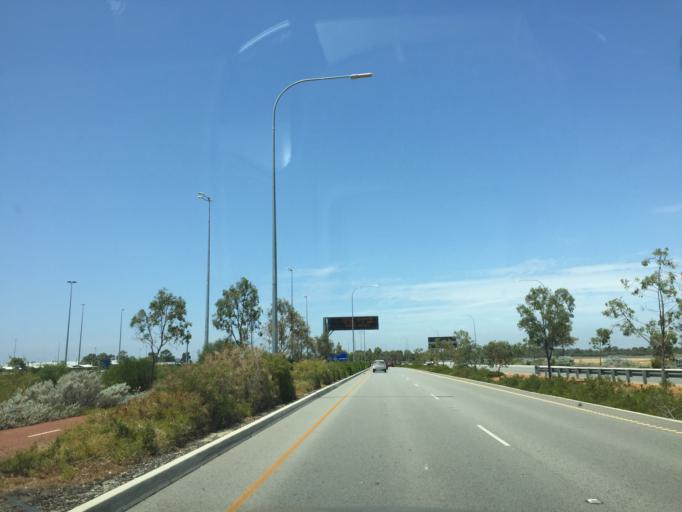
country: AU
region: Western Australia
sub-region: Belmont
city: Redcliffe
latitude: -31.9524
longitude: 115.9699
